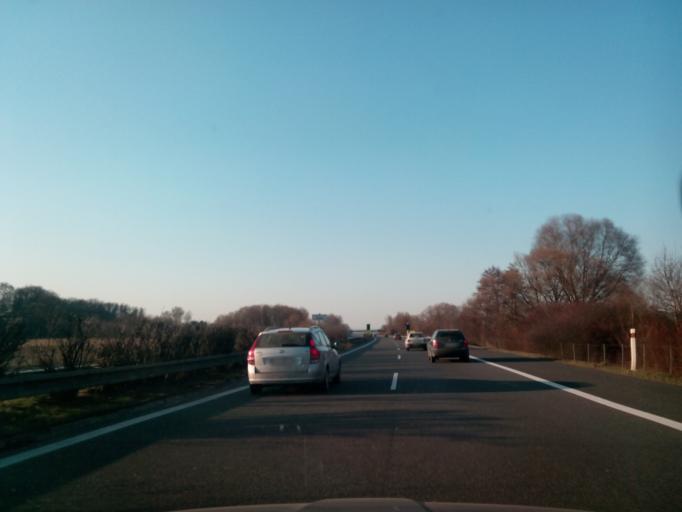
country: SK
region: Kosicky
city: Kosice
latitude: 48.7937
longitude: 21.3129
